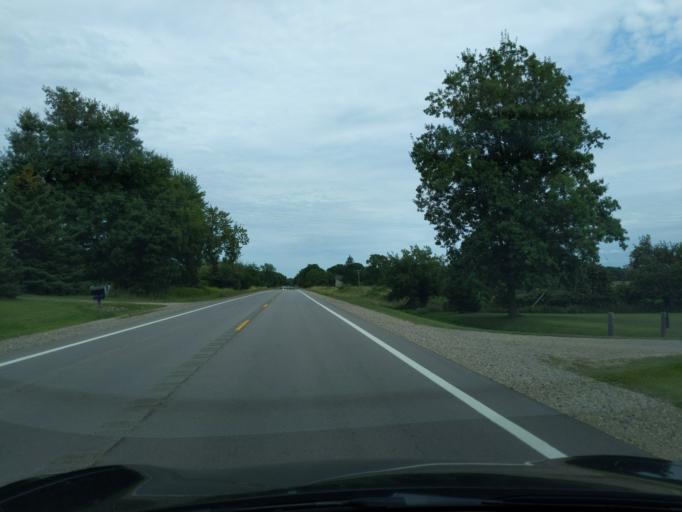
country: US
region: Michigan
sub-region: Barry County
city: Nashville
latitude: 42.5673
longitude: -85.0295
